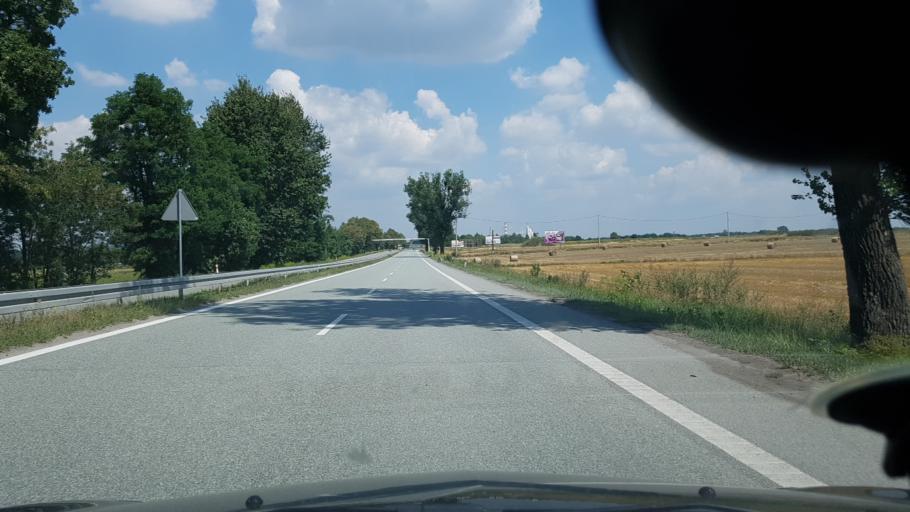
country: PL
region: Silesian Voivodeship
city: Gardawice
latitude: 50.1009
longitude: 18.7781
